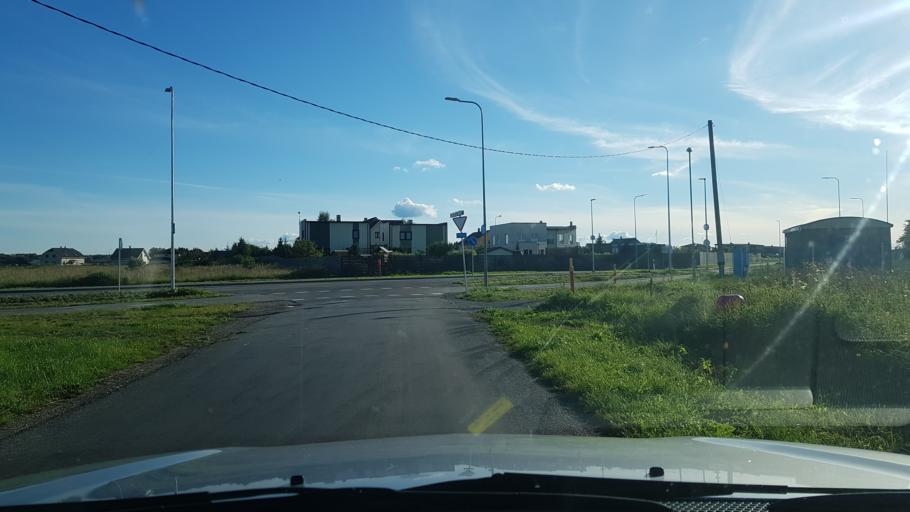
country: EE
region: Harju
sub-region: Rae vald
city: Jueri
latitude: 59.3878
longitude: 24.8511
